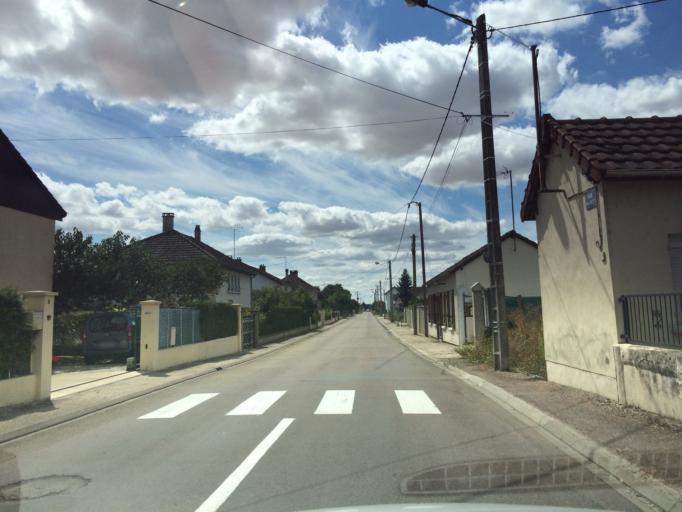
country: FR
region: Bourgogne
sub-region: Departement de l'Yonne
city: Laroche-Saint-Cydroine
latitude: 47.9561
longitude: 3.4998
